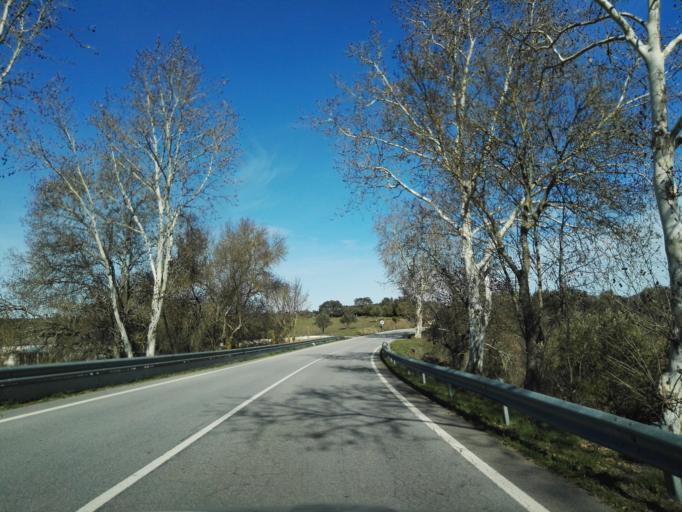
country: PT
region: Portalegre
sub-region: Arronches
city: Arronches
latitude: 39.1273
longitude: -7.2956
